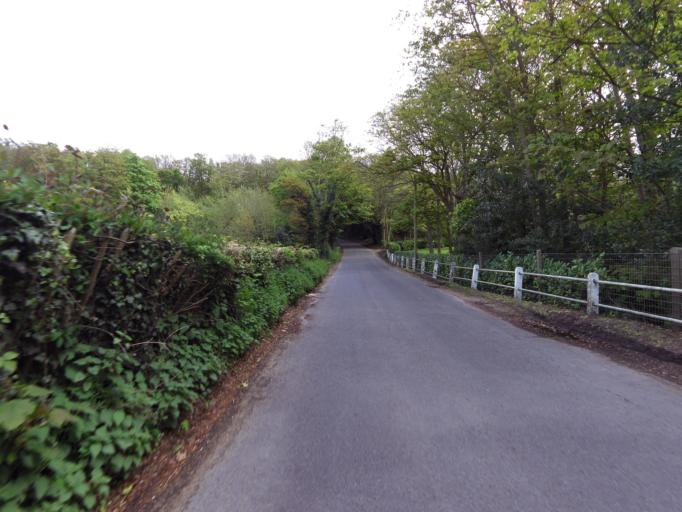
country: GB
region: England
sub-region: Suffolk
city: Ipswich
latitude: 51.9808
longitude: 1.1638
